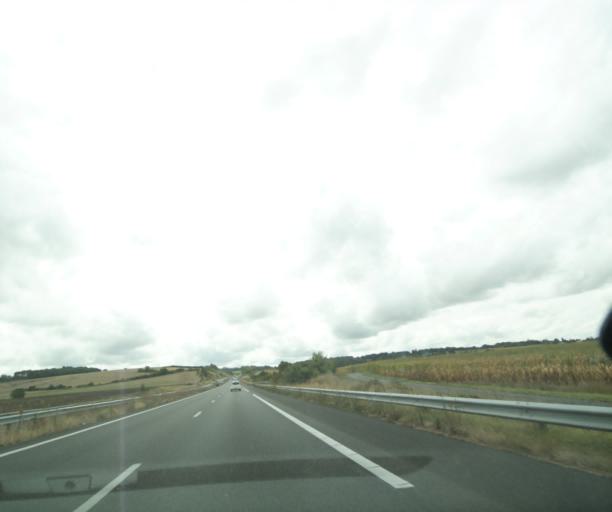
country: FR
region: Poitou-Charentes
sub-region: Departement de la Charente-Maritime
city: Mirambeau
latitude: 45.4194
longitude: -0.6036
